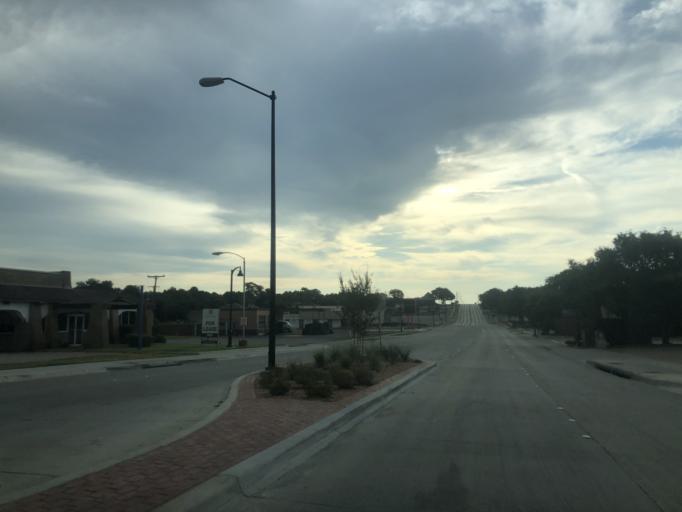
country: US
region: Texas
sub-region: Tarrant County
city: Hurst
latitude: 32.8236
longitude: -97.1790
